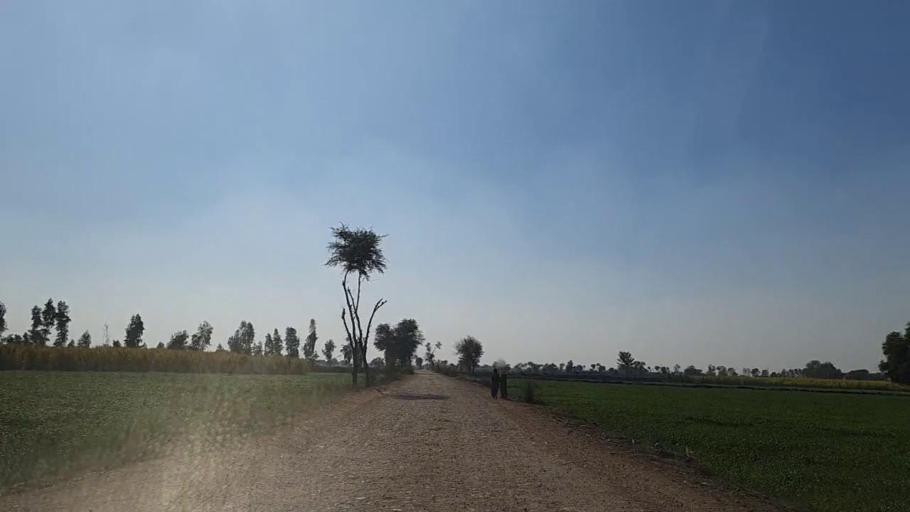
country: PK
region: Sindh
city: Bandhi
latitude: 26.5258
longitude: 68.2917
